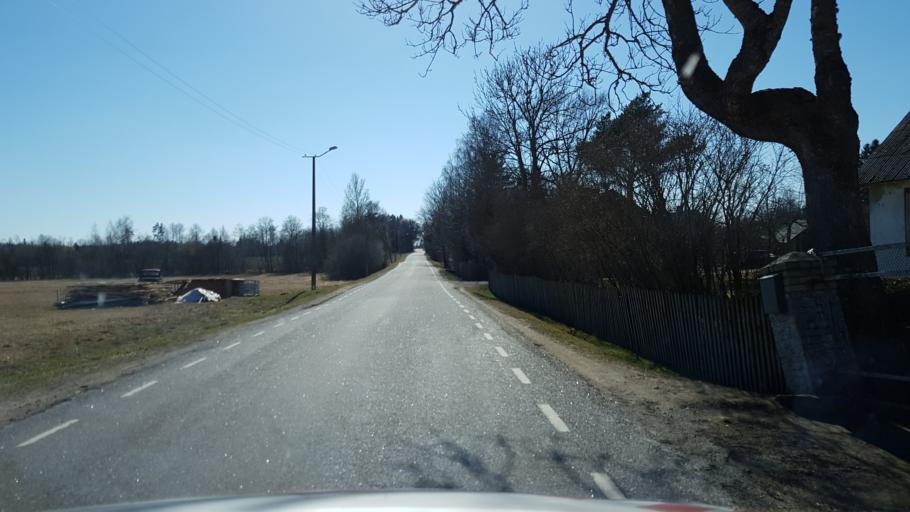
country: EE
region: Laeaene-Virumaa
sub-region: Tamsalu vald
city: Tamsalu
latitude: 59.0872
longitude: 26.1662
